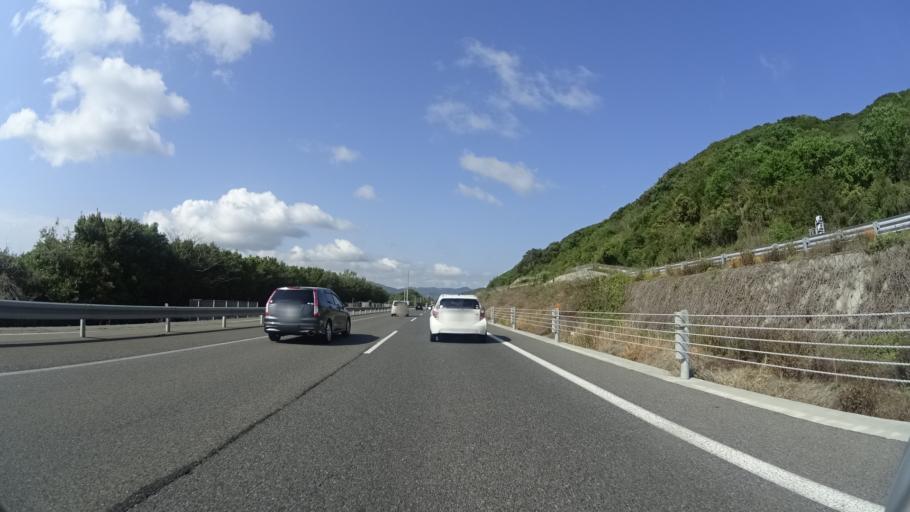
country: JP
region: Hyogo
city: Akashi
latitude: 34.5646
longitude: 135.0084
